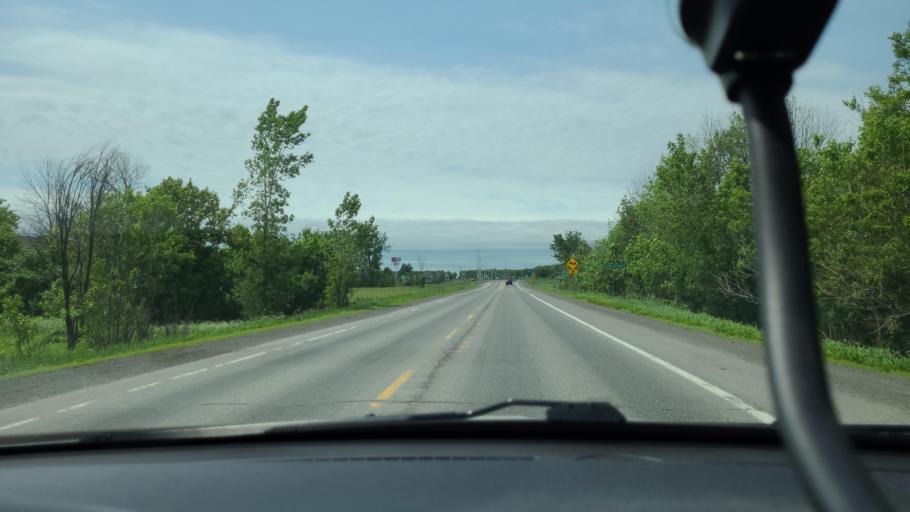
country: CA
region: Quebec
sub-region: Lanaudiere
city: Saint-Jacques
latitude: 45.9572
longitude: -73.5736
